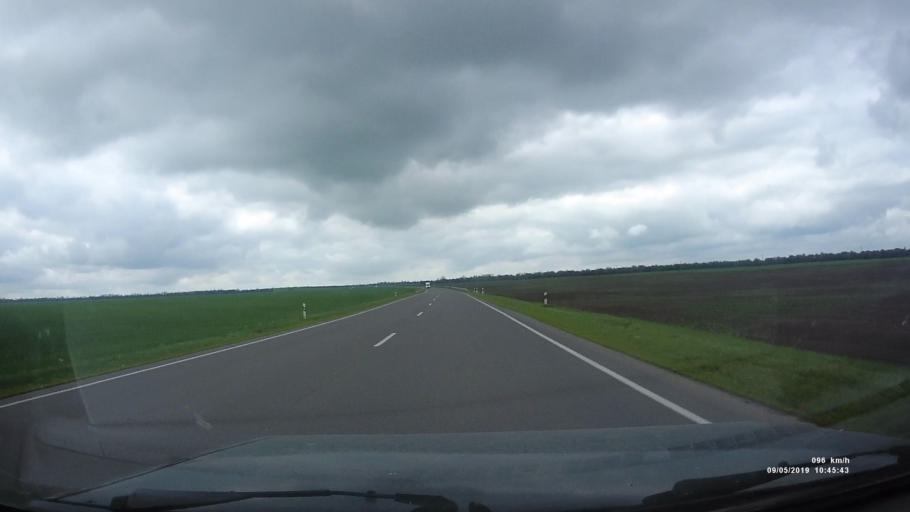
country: RU
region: Rostov
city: Peshkovo
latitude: 46.9930
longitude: 39.3633
